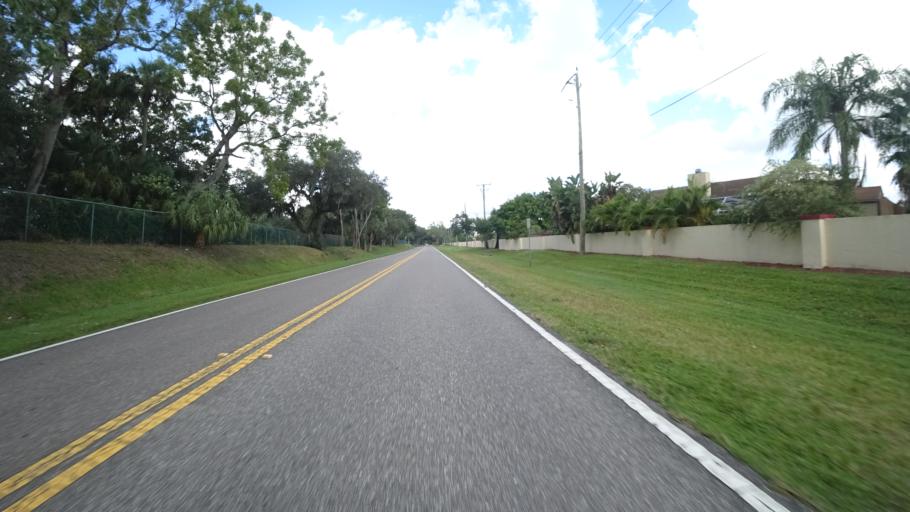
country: US
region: Florida
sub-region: Manatee County
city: Samoset
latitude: 27.4366
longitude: -82.5136
